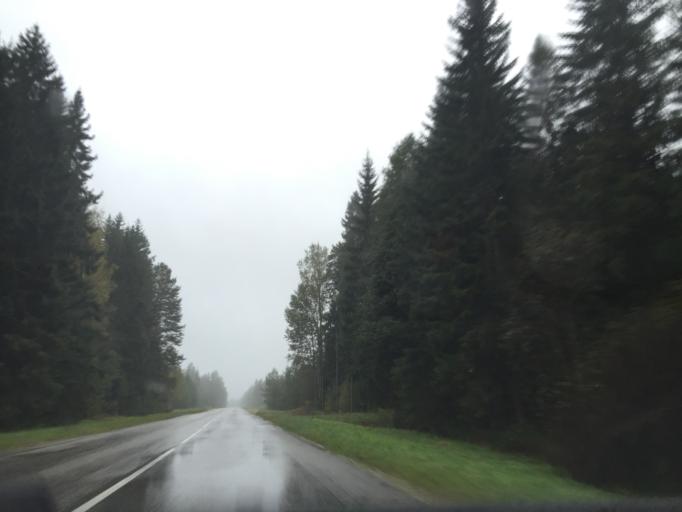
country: LV
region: Ropazu
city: Ropazi
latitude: 57.0096
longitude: 24.6787
